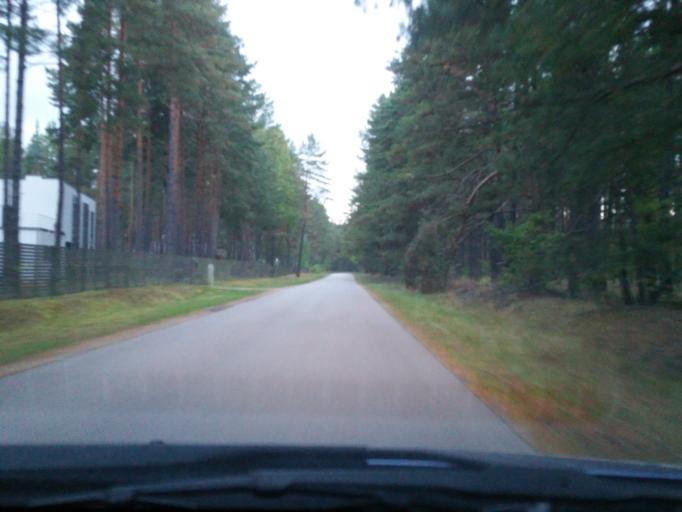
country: LV
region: Adazi
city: Adazi
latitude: 57.1237
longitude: 24.3436
